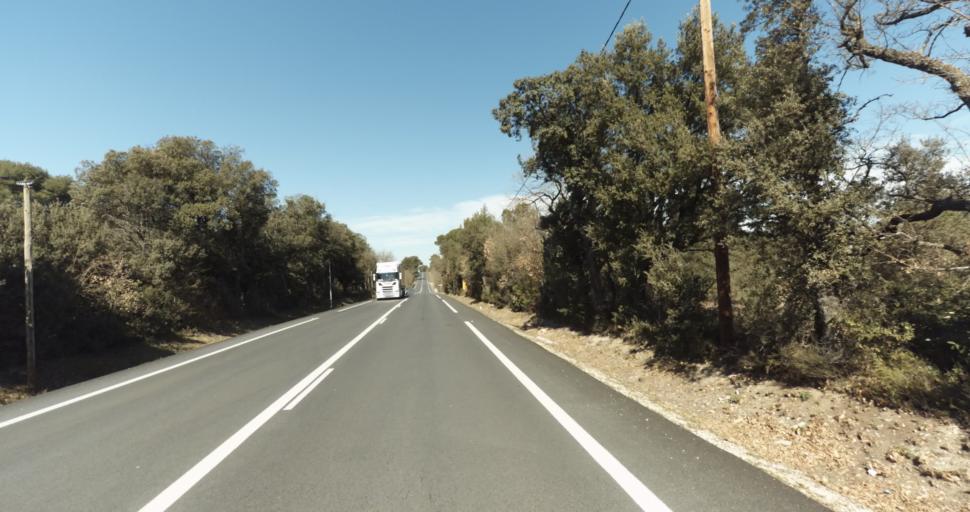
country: FR
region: Provence-Alpes-Cote d'Azur
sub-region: Departement des Bouches-du-Rhone
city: Eguilles
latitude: 43.5987
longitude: 5.3488
